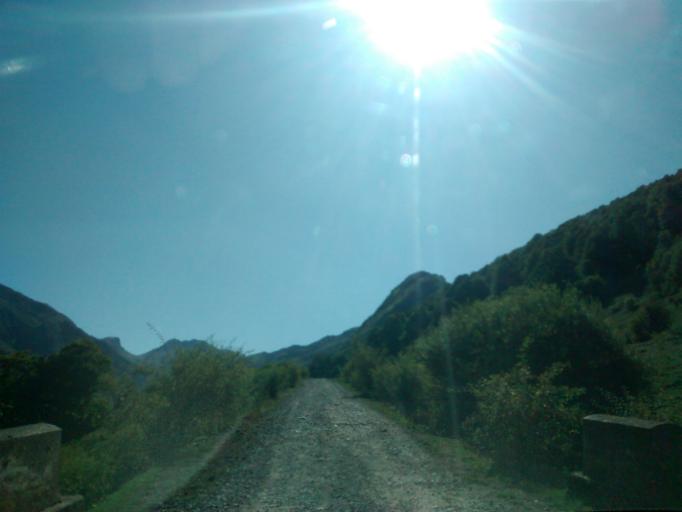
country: ES
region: Aragon
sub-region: Provincia de Huesca
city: Aragues del Puerto
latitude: 42.8497
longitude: -0.6724
